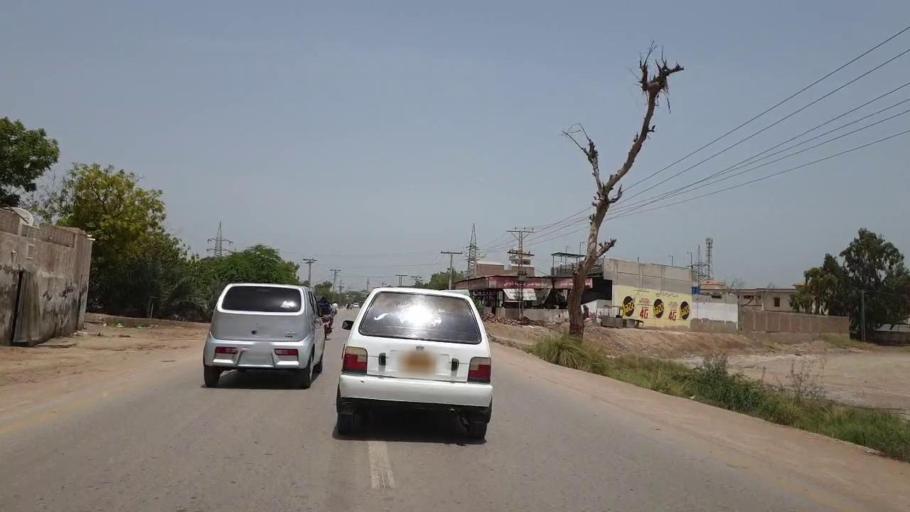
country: PK
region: Sindh
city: Nawabshah
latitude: 26.2490
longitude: 68.4292
